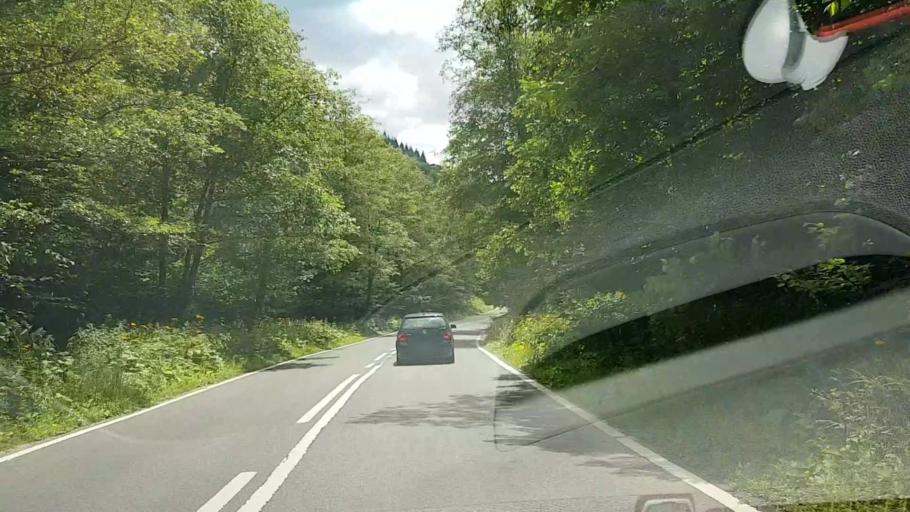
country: RO
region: Suceava
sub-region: Comuna Crucea
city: Crucea
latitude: 47.2987
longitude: 25.6320
